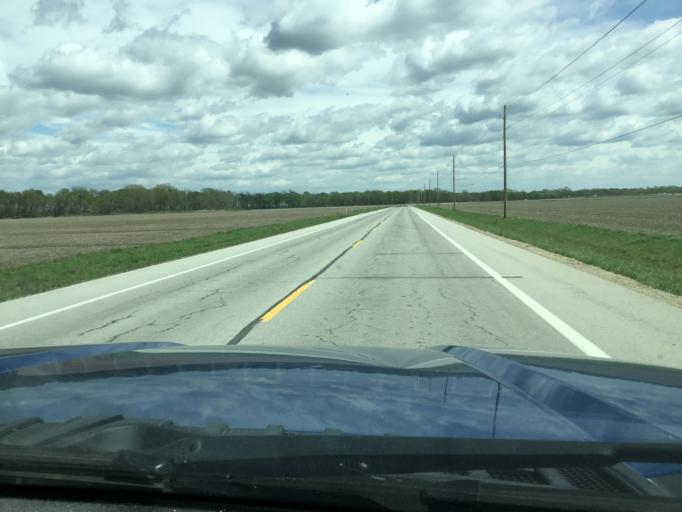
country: US
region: Kansas
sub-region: Douglas County
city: Lawrence
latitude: 38.9136
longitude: -95.2762
